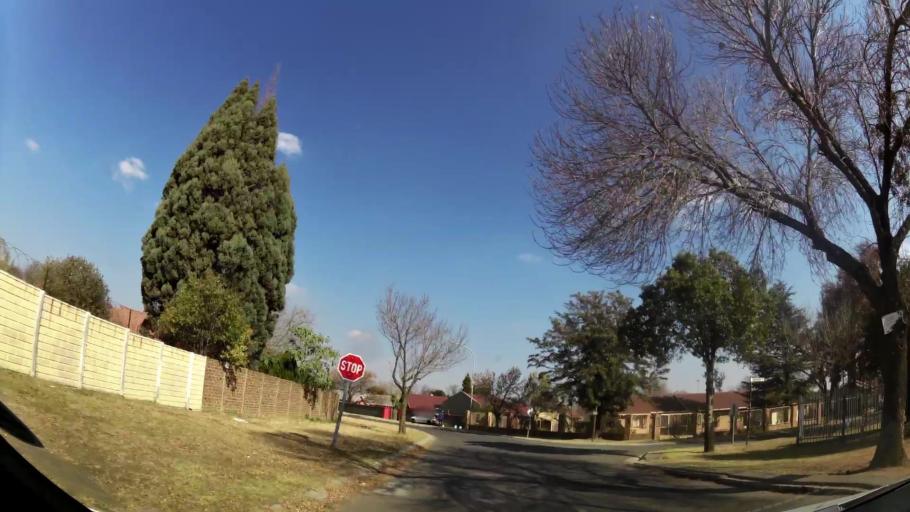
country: ZA
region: Gauteng
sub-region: Ekurhuleni Metropolitan Municipality
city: Benoni
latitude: -26.2432
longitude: 28.3109
